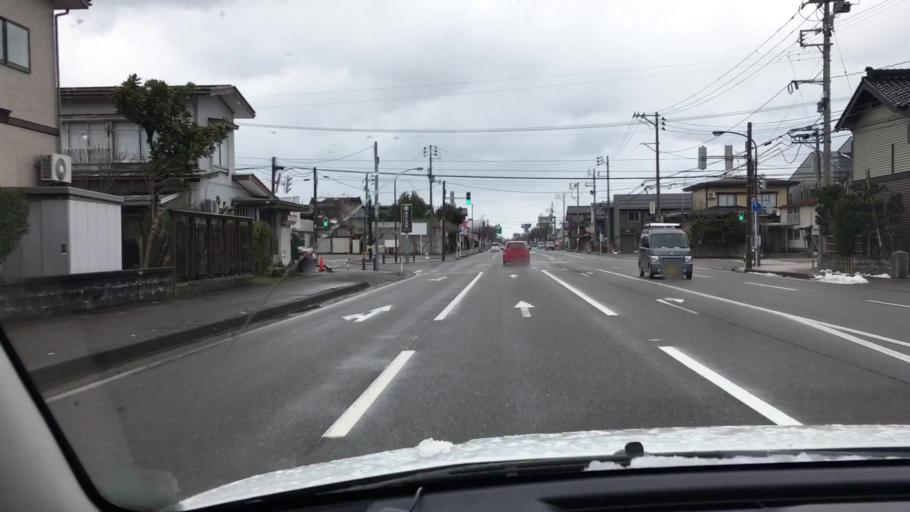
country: JP
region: Niigata
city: Joetsu
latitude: 37.1435
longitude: 138.2285
